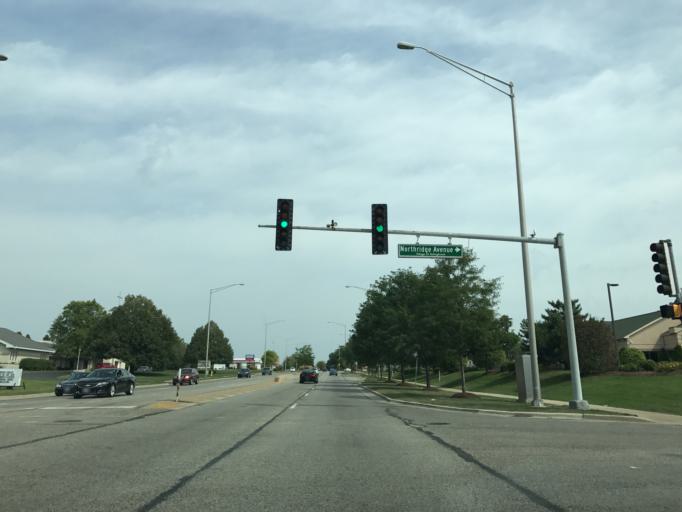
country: US
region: Illinois
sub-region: Will County
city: Bolingbrook
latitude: 41.7015
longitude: -88.0683
